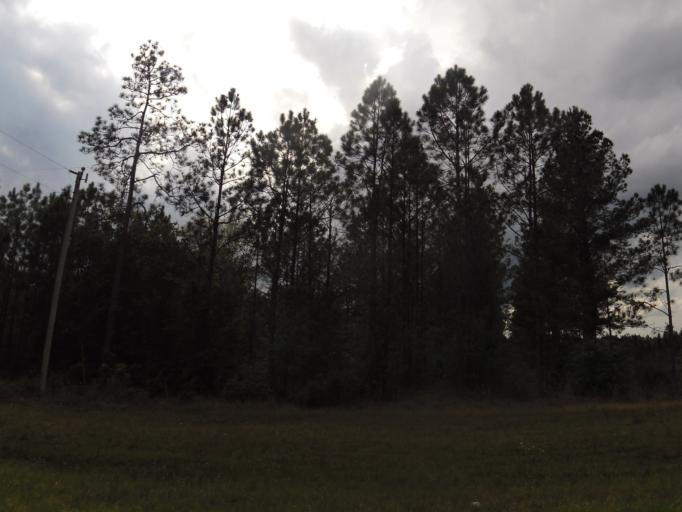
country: US
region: Georgia
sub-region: Charlton County
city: Folkston
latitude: 30.8958
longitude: -82.0166
